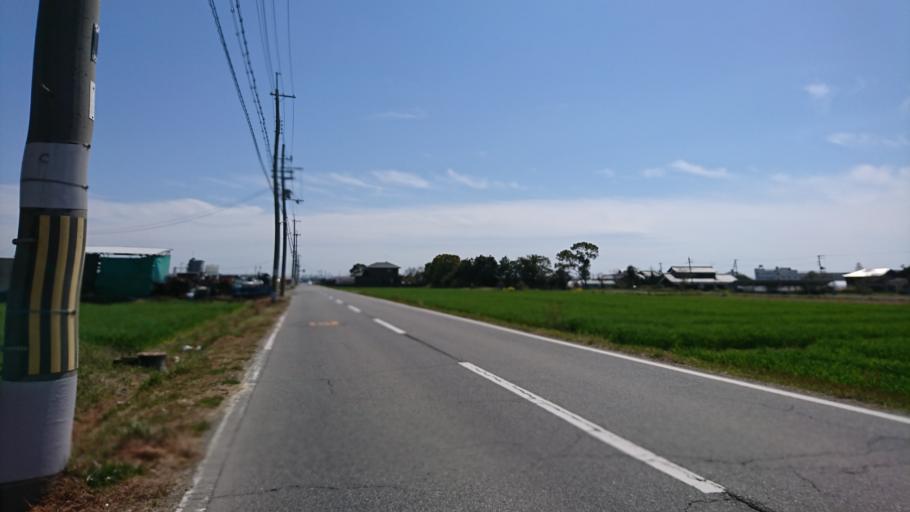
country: JP
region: Hyogo
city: Kakogawacho-honmachi
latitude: 34.7516
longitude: 134.8860
